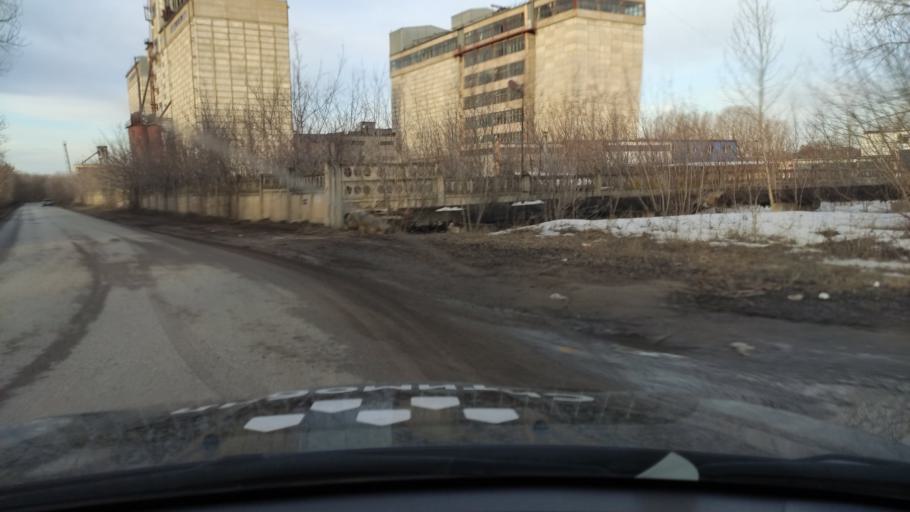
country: RU
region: Samara
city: Povolzhskiy
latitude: 53.5743
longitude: 49.6840
